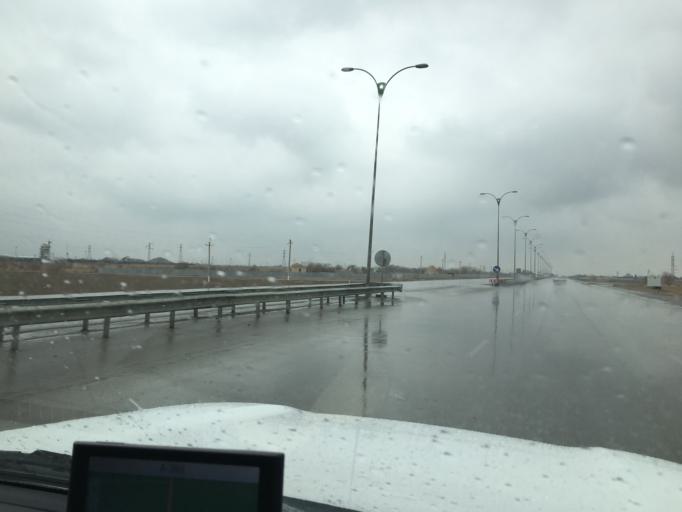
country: TM
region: Mary
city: Mary
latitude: 37.5412
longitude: 61.8770
